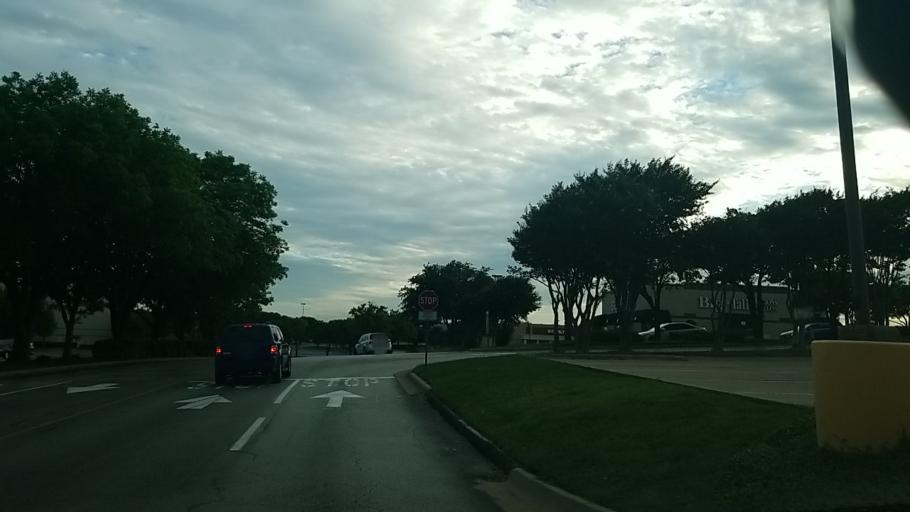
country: US
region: Texas
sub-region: Denton County
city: Lewisville
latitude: 33.0048
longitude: -96.9729
